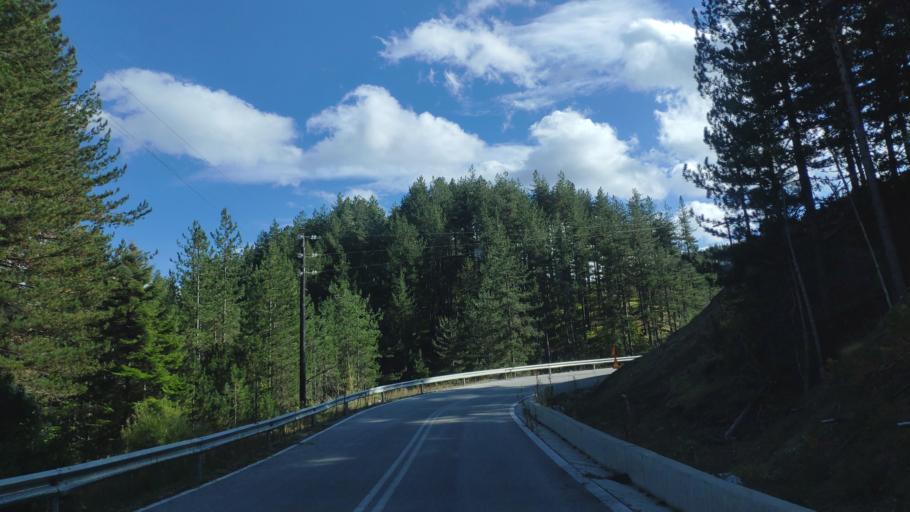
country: AL
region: Korce
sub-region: Rrethi i Devollit
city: Miras
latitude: 40.4082
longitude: 20.8776
